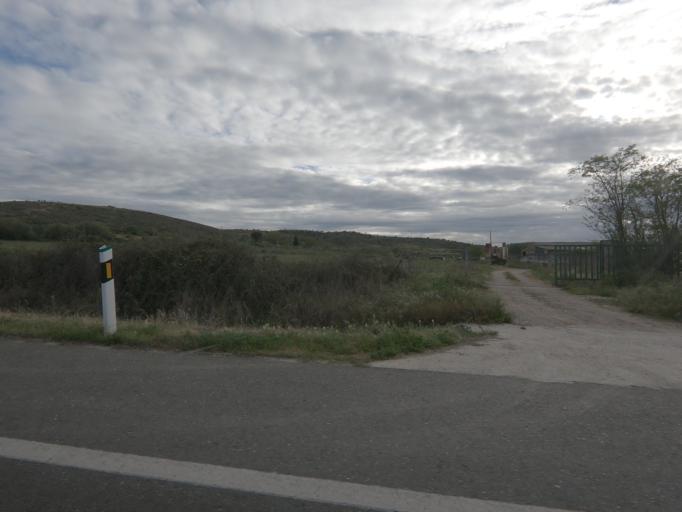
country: ES
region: Extremadura
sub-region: Provincia de Caceres
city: Coria
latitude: 39.9608
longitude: -6.5147
